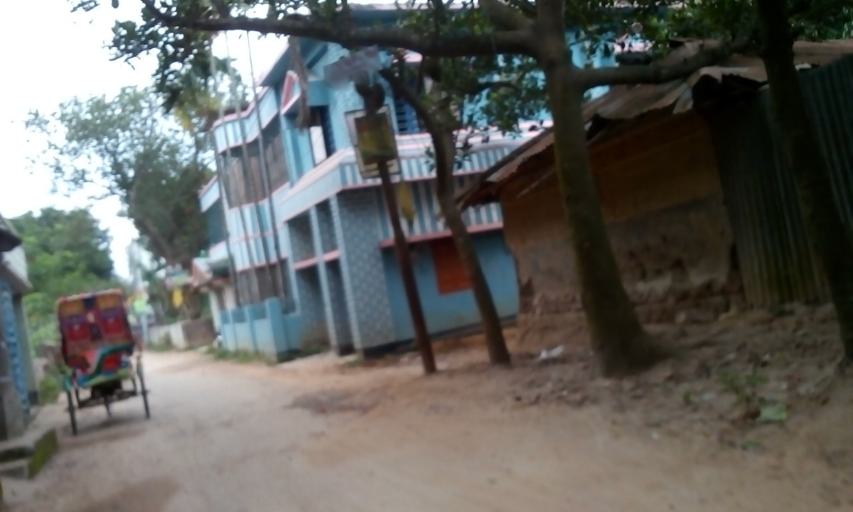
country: IN
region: West Bengal
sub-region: Dakshin Dinajpur
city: Balurghat
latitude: 25.3845
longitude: 88.9934
